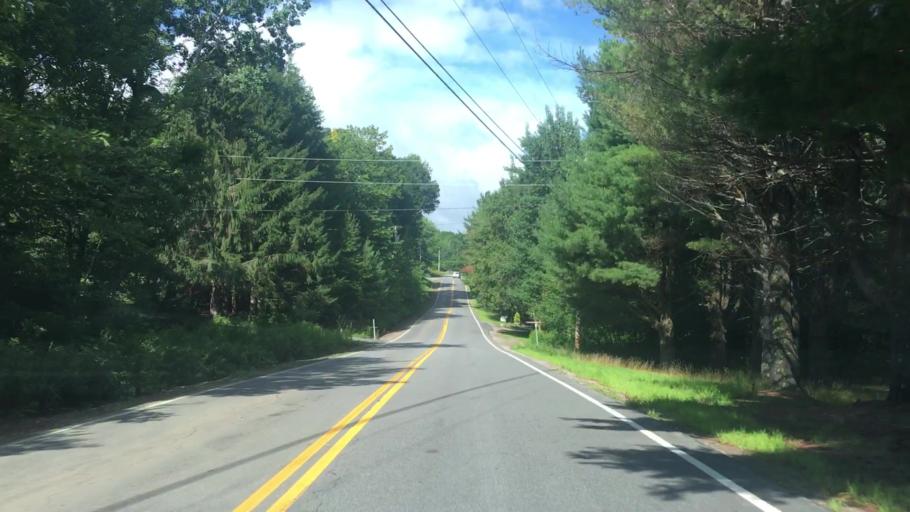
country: US
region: New Hampshire
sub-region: Belknap County
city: Gilford
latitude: 43.5290
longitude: -71.3321
